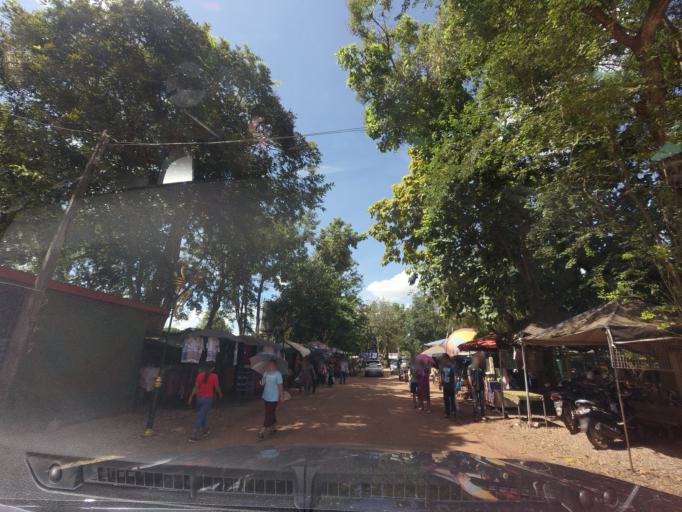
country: TH
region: Changwat Udon Thani
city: Ban Dung
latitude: 17.7422
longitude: 103.3587
